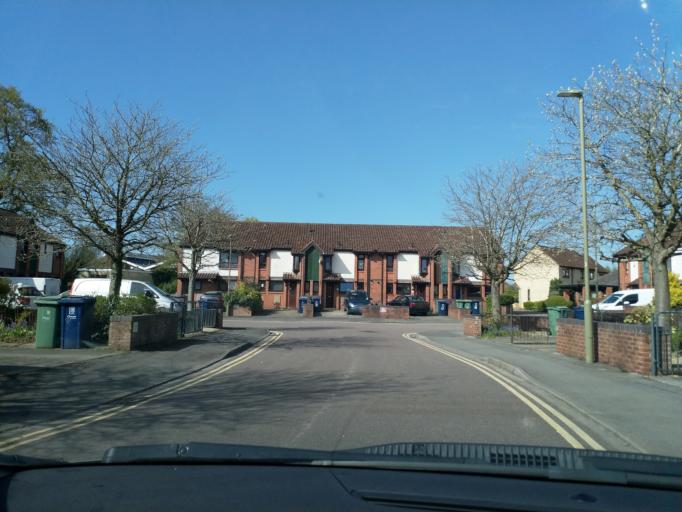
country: GB
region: England
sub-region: Oxfordshire
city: Cowley
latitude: 51.7559
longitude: -1.2090
